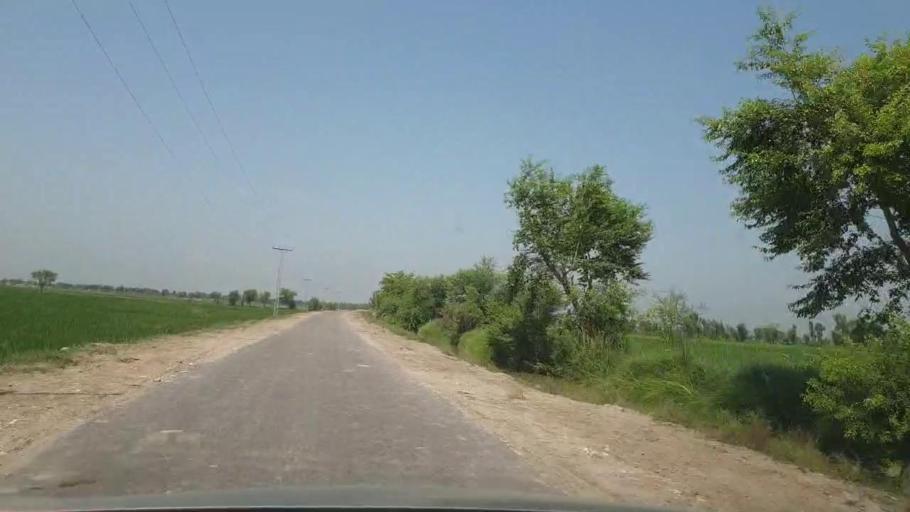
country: PK
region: Sindh
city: Warah
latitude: 27.4734
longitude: 67.7612
